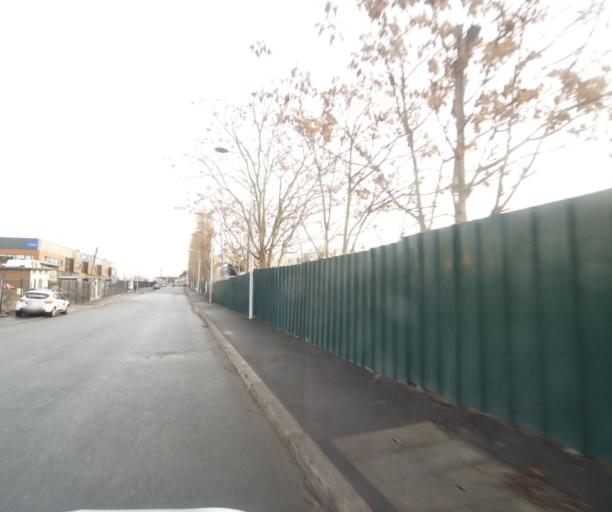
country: FR
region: Ile-de-France
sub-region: Departement des Yvelines
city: Carrieres-sur-Seine
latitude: 48.8954
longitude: 2.1834
